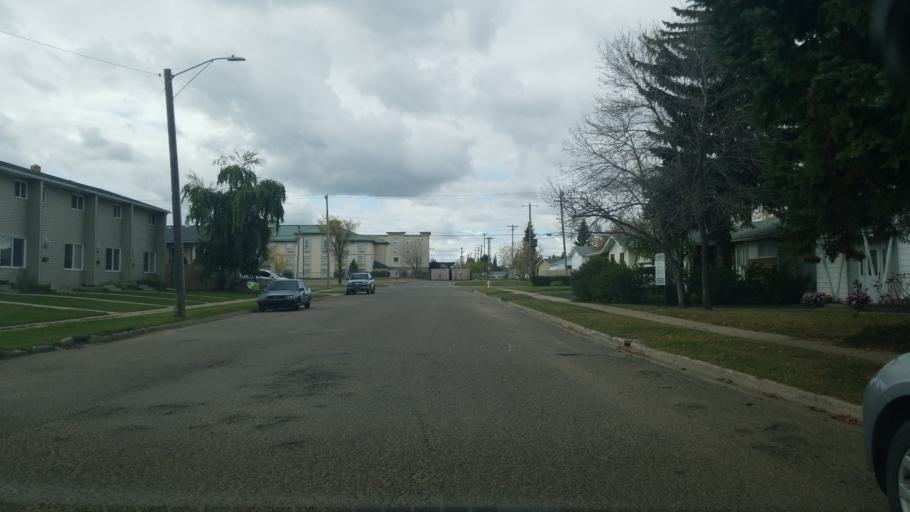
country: CA
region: Saskatchewan
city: Lloydminster
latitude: 53.2790
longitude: -110.0184
